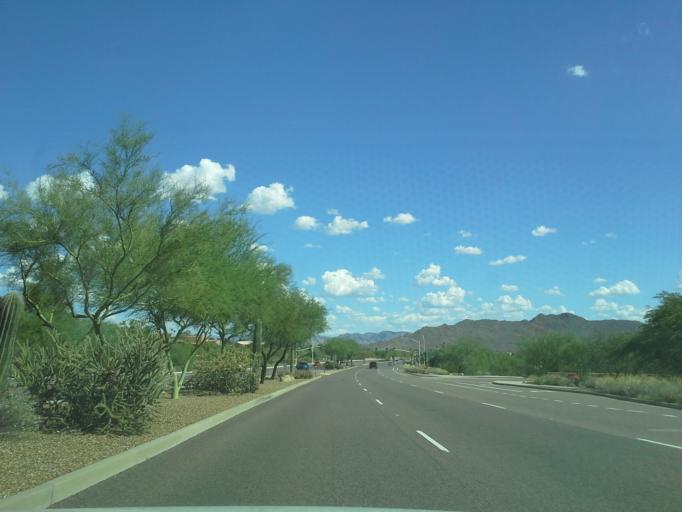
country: US
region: Arizona
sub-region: Maricopa County
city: Fountain Hills
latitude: 33.5773
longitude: -111.7226
